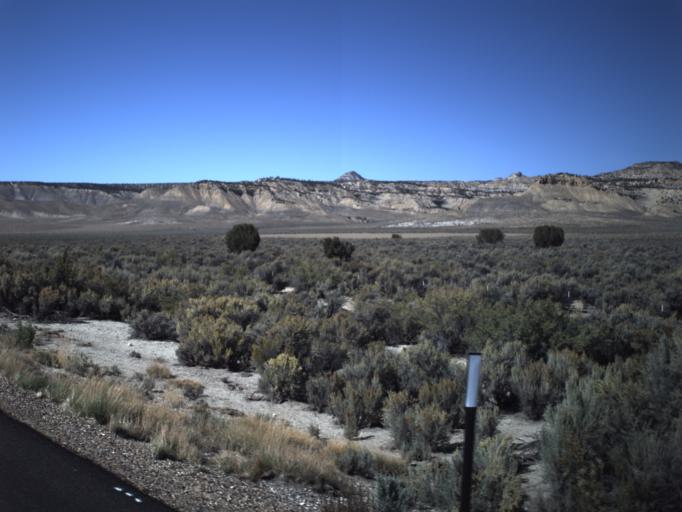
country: US
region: Utah
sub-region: Garfield County
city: Panguitch
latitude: 37.5983
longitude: -111.9510
